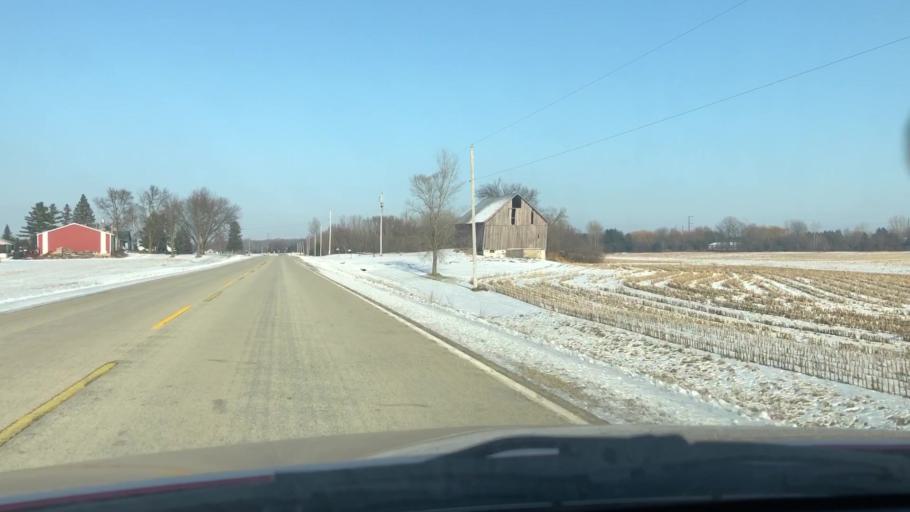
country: US
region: Wisconsin
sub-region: Outagamie County
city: Seymour
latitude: 44.4228
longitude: -88.3676
